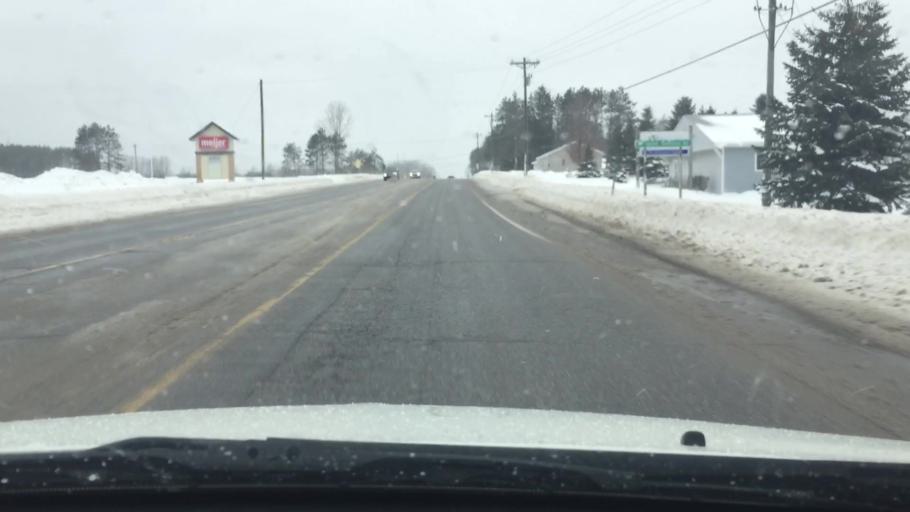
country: US
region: Michigan
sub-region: Otsego County
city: Gaylord
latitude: 45.0279
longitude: -84.7249
